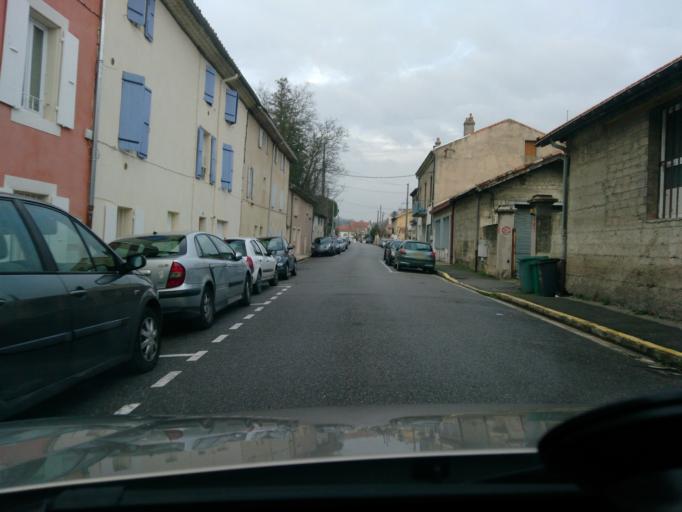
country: FR
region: Rhone-Alpes
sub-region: Departement de la Drome
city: Montelimar
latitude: 44.5600
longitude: 4.7569
